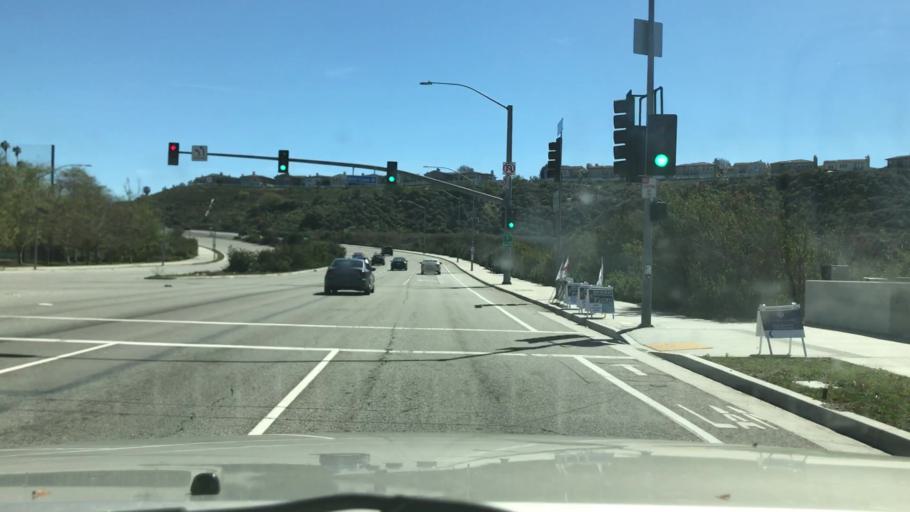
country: US
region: California
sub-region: Los Angeles County
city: Marina del Rey
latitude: 33.9678
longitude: -118.4278
